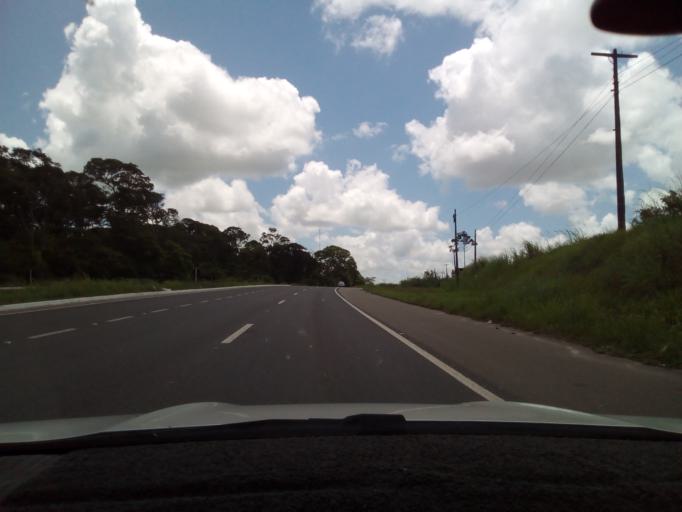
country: BR
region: Paraiba
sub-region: Santa Rita
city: Santa Rita
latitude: -7.1438
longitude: -34.9966
